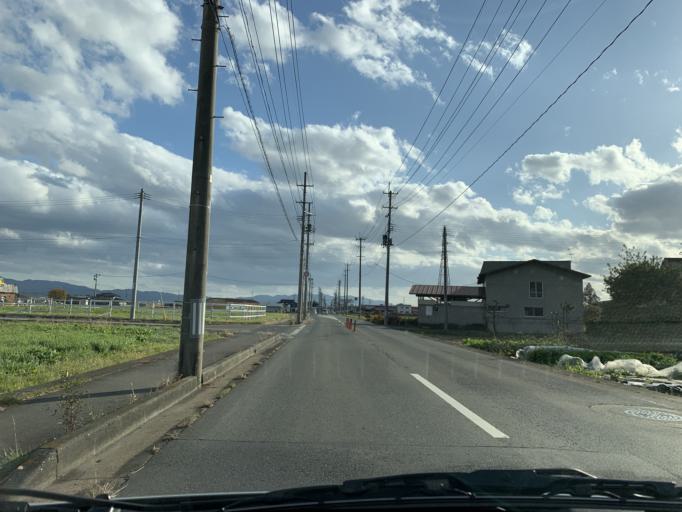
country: JP
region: Iwate
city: Mizusawa
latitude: 39.1567
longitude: 141.1580
